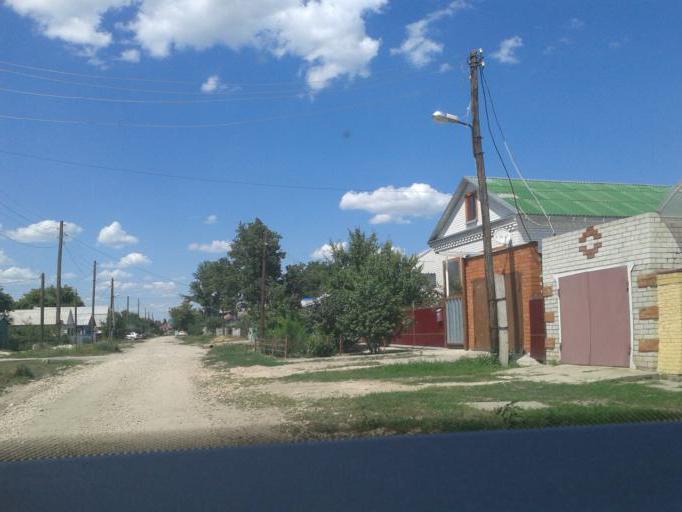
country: RU
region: Volgograd
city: Frolovo
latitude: 49.7610
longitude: 43.6620
